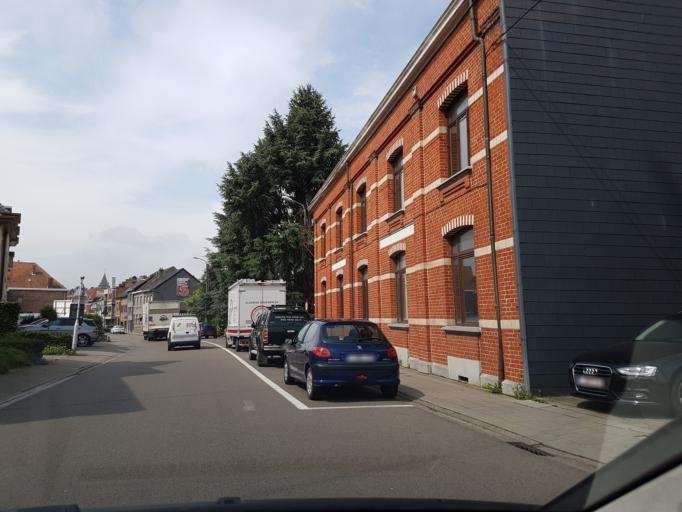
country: BE
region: Flanders
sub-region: Provincie Vlaams-Brabant
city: Meise
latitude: 50.9533
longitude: 4.3121
